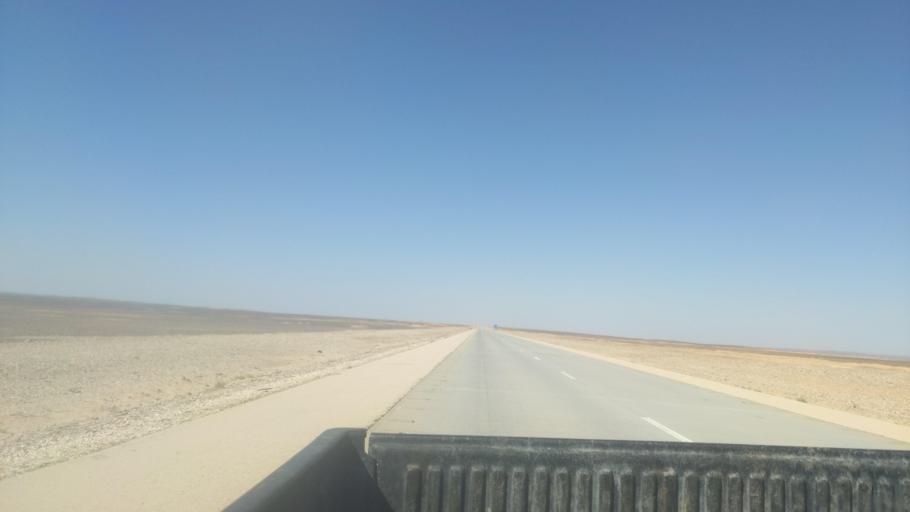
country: JO
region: Amman
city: Al Azraq ash Shamali
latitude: 31.4444
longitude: 36.7599
